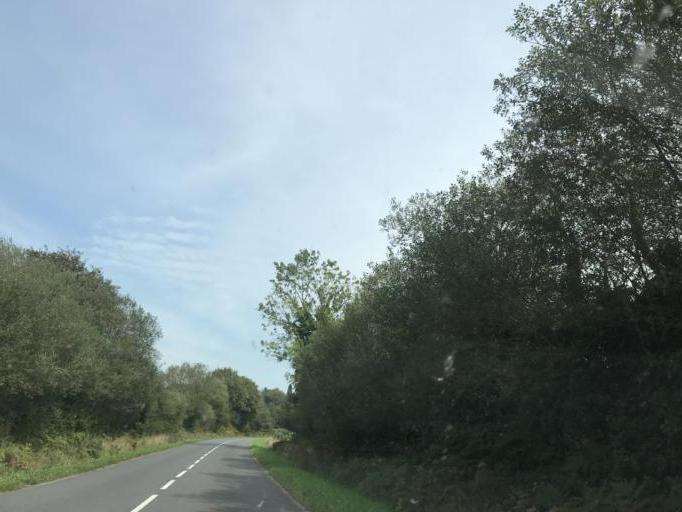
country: FR
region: Brittany
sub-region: Departement du Finistere
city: Plouneour-Menez
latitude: 48.3545
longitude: -3.8591
